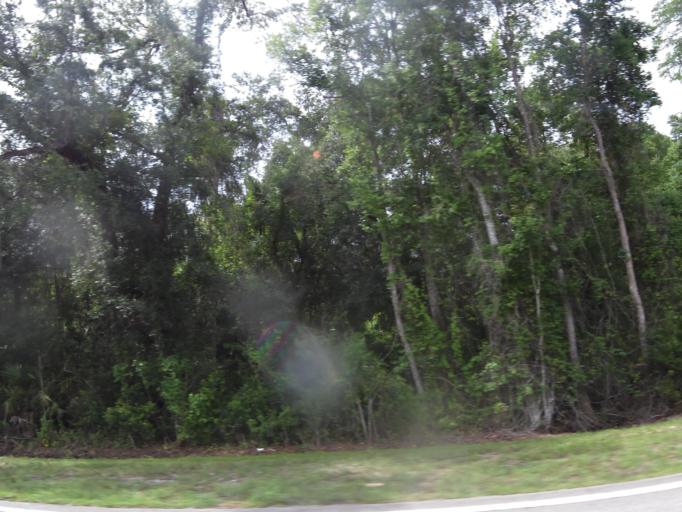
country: US
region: Florida
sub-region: Saint Johns County
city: Saint Augustine South
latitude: 29.8597
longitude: -81.4112
